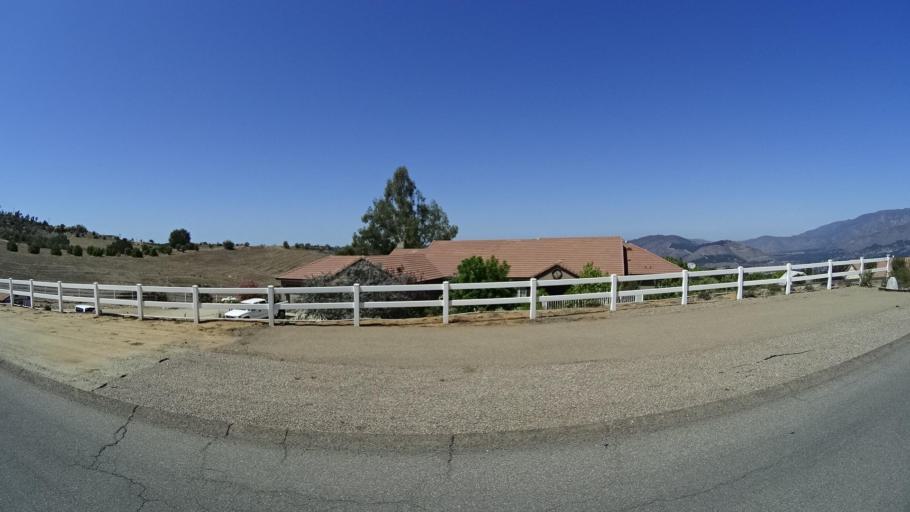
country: US
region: California
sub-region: San Diego County
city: Valley Center
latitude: 33.2855
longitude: -116.9916
